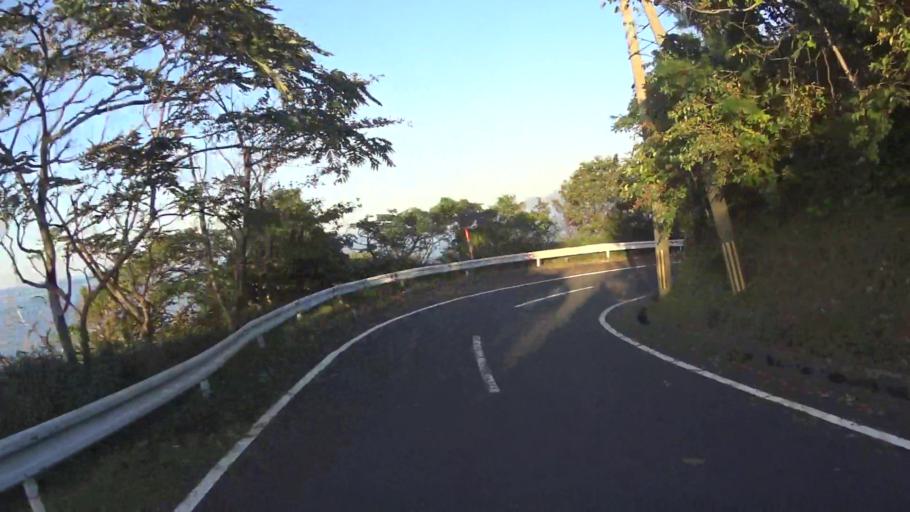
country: JP
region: Hyogo
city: Toyooka
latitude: 35.6916
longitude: 134.9870
